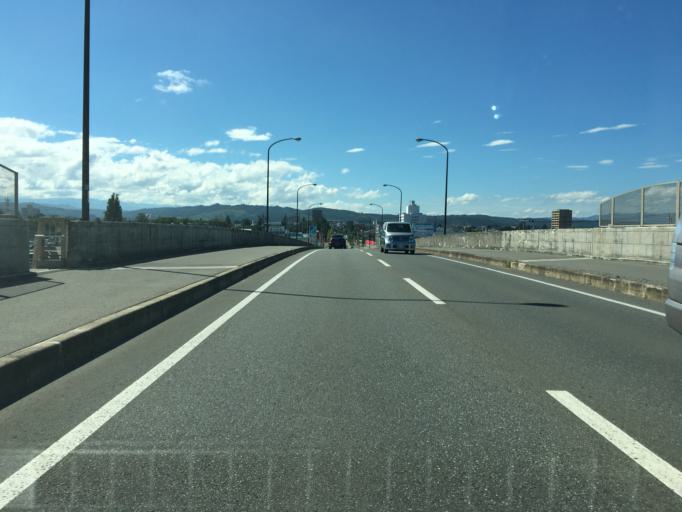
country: JP
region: Yamagata
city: Yonezawa
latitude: 37.9197
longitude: 140.1251
